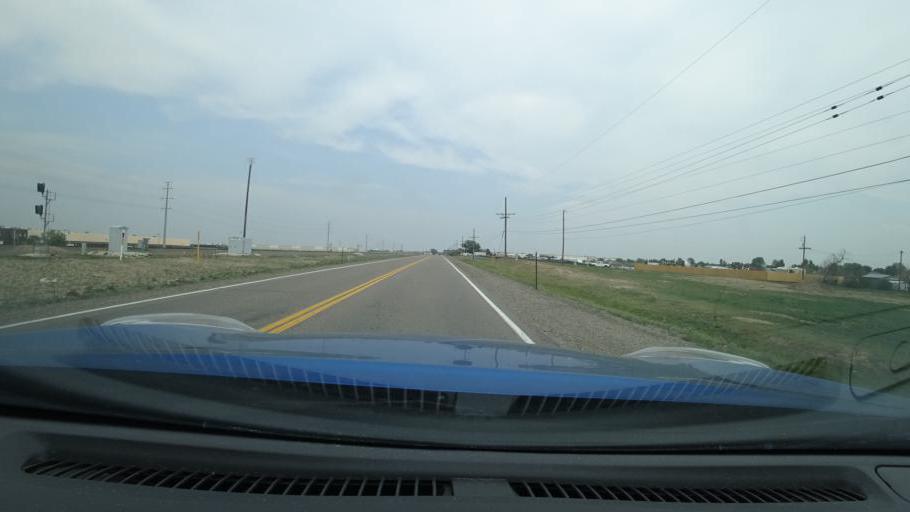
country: US
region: Colorado
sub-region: Adams County
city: Aurora
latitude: 39.7537
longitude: -104.7705
